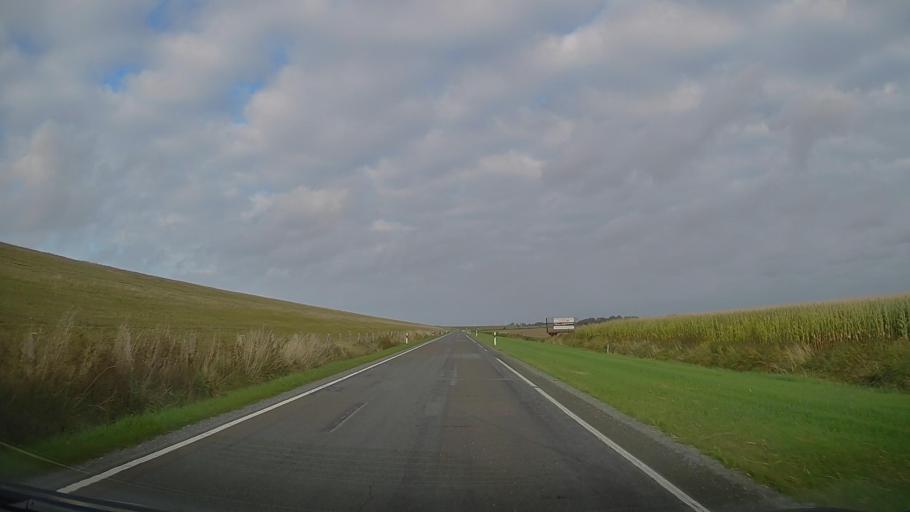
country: DE
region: Schleswig-Holstein
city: Uelvesbull
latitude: 54.4112
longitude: 8.8954
